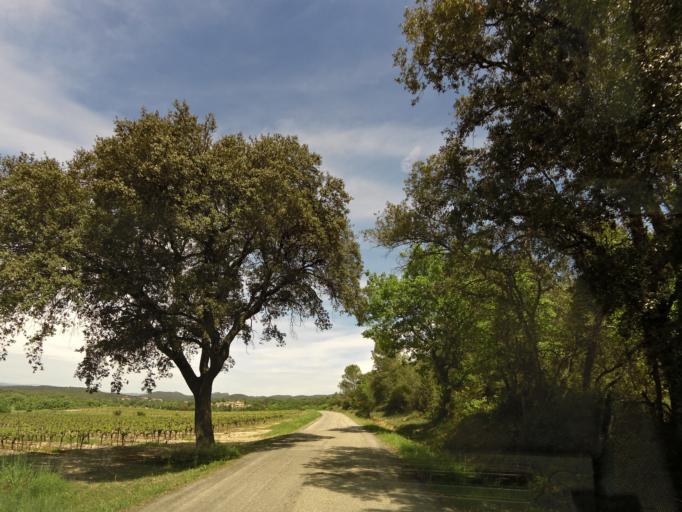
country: FR
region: Languedoc-Roussillon
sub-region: Departement du Gard
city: Quissac
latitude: 43.8690
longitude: 4.0286
